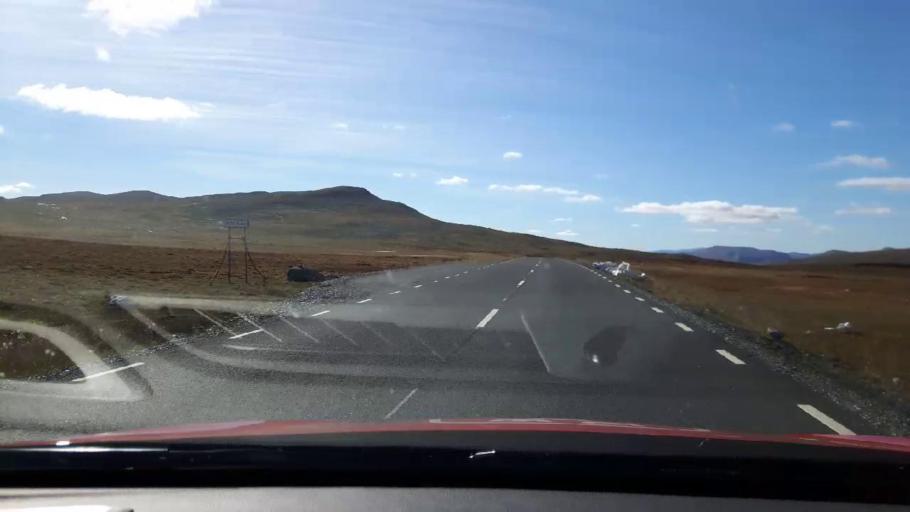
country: NO
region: Nordland
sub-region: Hattfjelldal
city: Hattfjelldal
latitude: 65.0638
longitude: 14.3800
